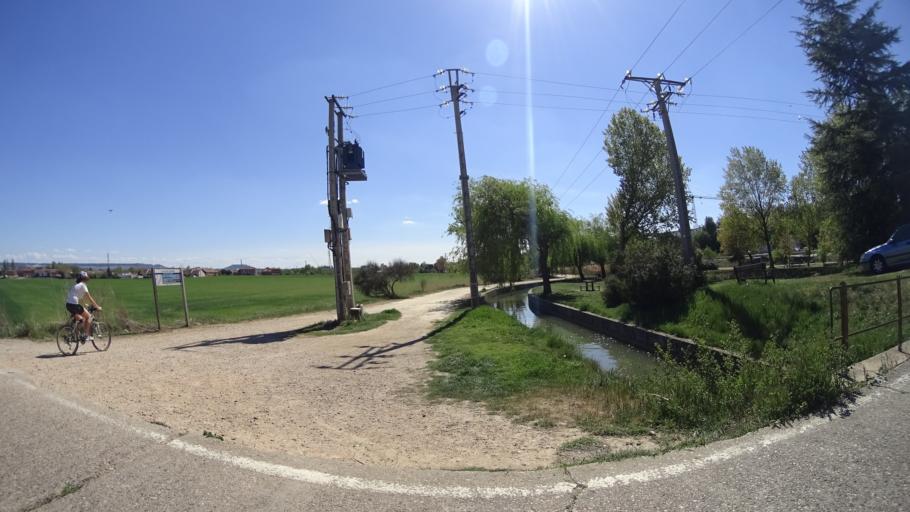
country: ES
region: Castille and Leon
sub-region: Provincia de Valladolid
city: Santovenia de Pisuerga
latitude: 41.6960
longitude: -4.7136
